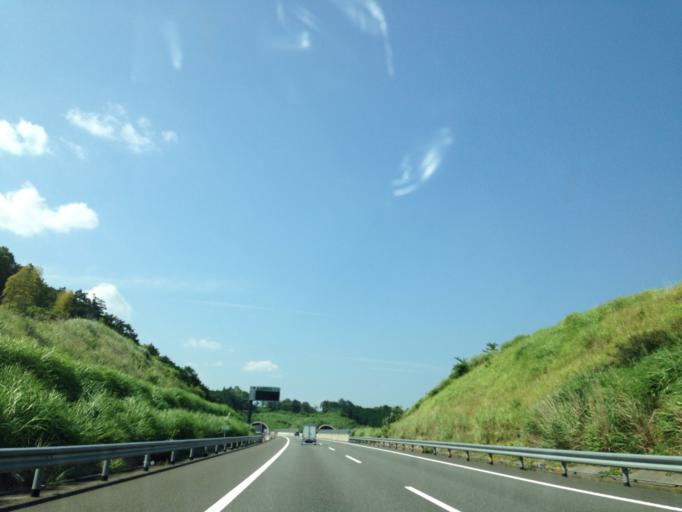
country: JP
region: Shizuoka
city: Mishima
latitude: 35.1896
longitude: 138.8888
